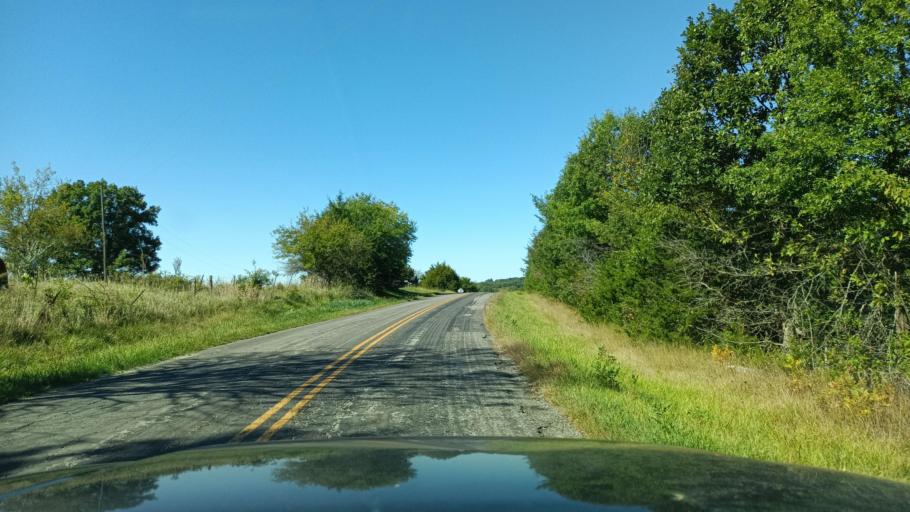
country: US
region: Missouri
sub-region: Scotland County
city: Memphis
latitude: 40.3499
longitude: -92.3150
